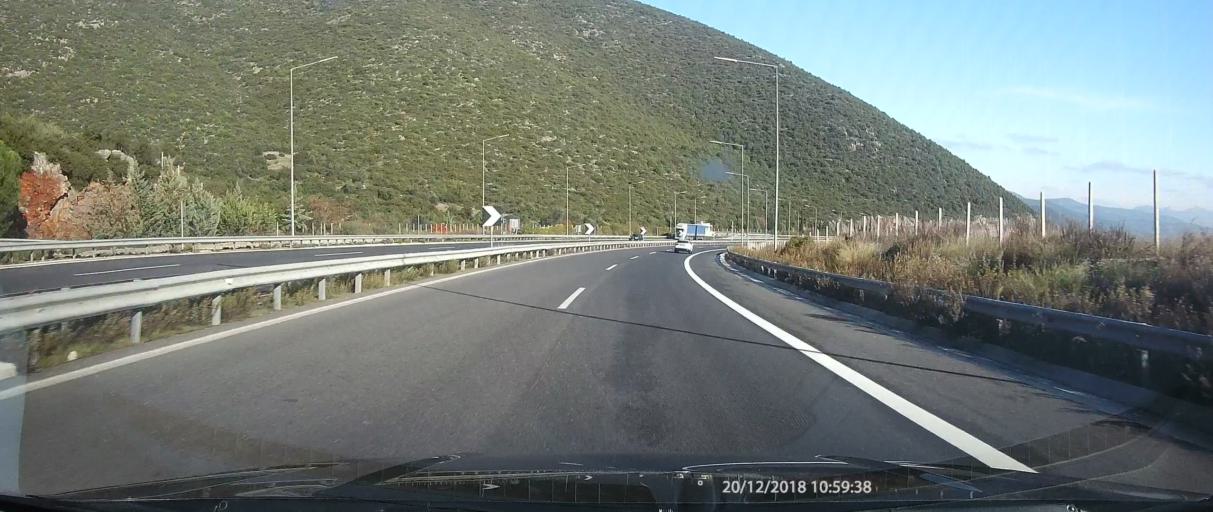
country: GR
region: Peloponnese
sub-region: Nomos Korinthias
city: Nemea
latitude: 37.7009
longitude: 22.5347
